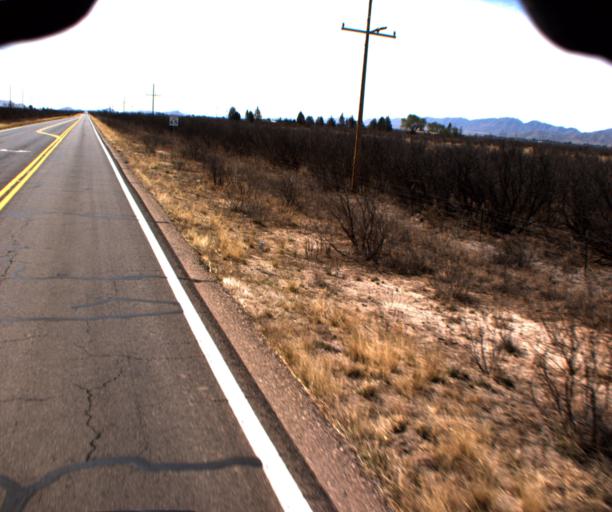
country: US
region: Arizona
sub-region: Cochise County
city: Willcox
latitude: 32.0351
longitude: -109.8786
